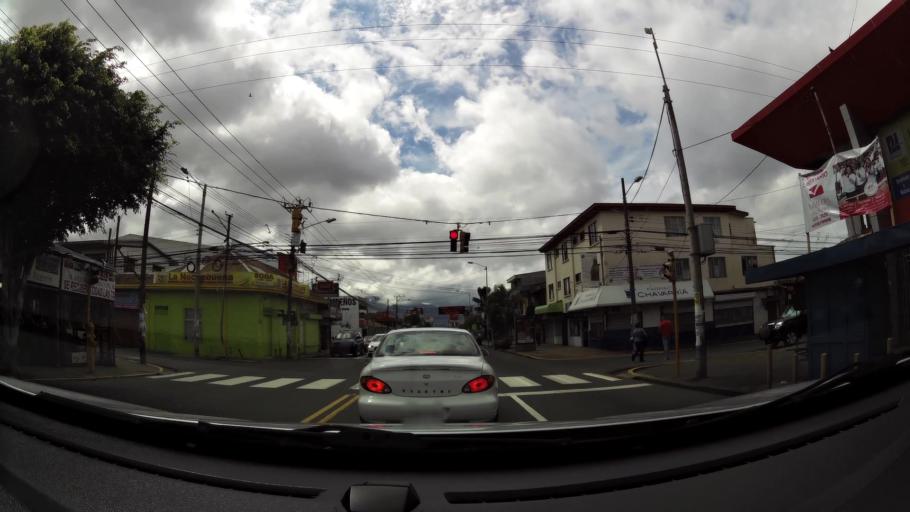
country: CR
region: San Jose
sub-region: Canton de Goicoechea
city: Guadalupe
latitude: 9.9459
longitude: -84.0551
